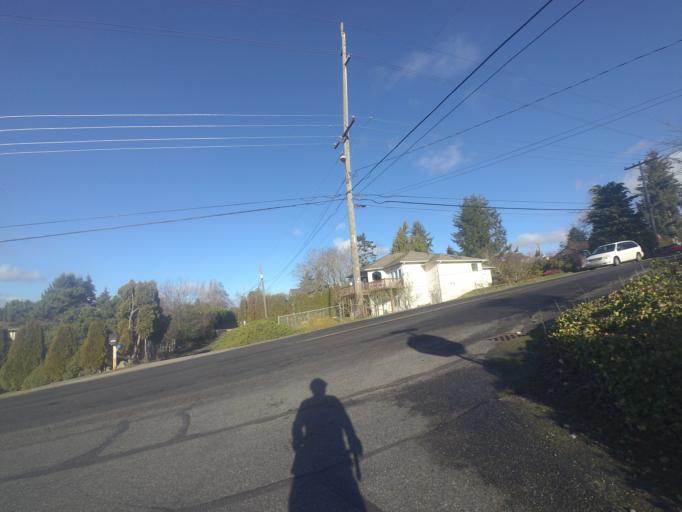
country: US
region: Washington
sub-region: Pierce County
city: University Place
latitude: 47.2280
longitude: -122.5464
